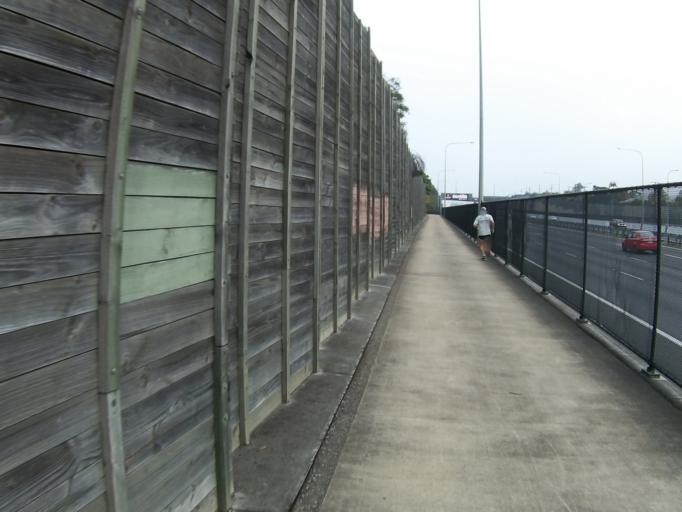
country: AU
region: Queensland
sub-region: Brisbane
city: Nathan
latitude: -27.5582
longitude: 153.0734
